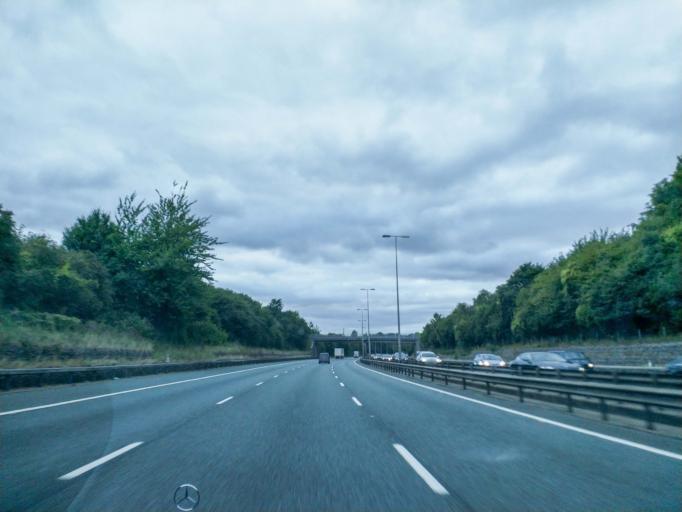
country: GB
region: England
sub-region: Buckinghamshire
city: Stokenchurch
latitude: 51.6266
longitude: -0.8556
